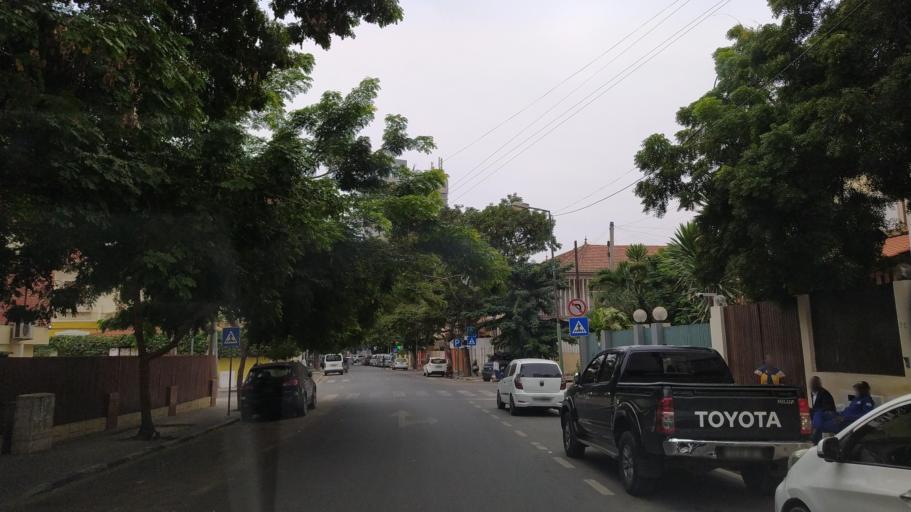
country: AO
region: Luanda
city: Luanda
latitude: -8.8195
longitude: 13.2402
